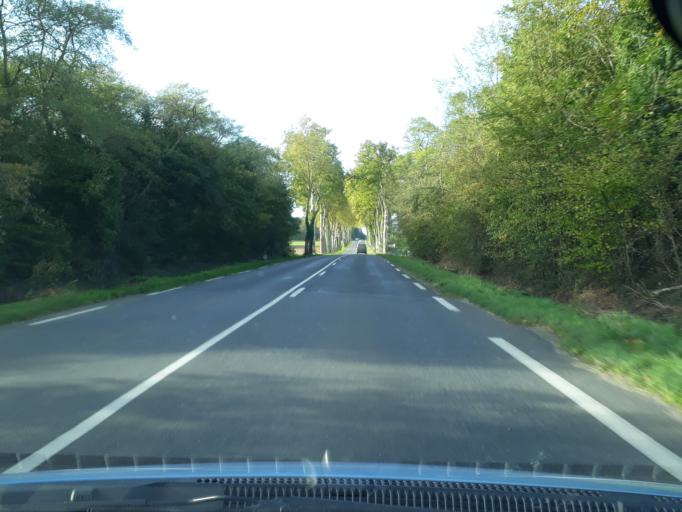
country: FR
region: Ile-de-France
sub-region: Departement de Seine-et-Marne
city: La Chapelle-la-Reine
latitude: 48.3263
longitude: 2.5834
